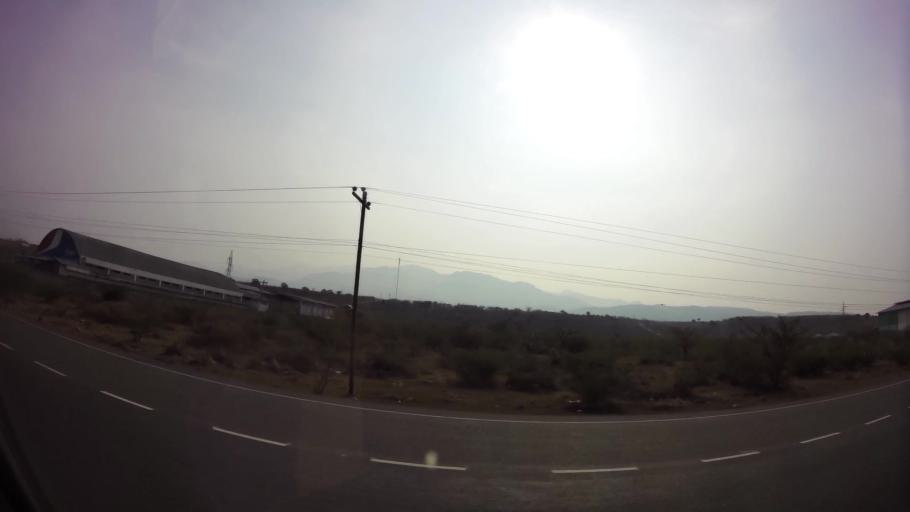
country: HN
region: Comayagua
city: Comayagua
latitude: 14.4154
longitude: -87.6245
